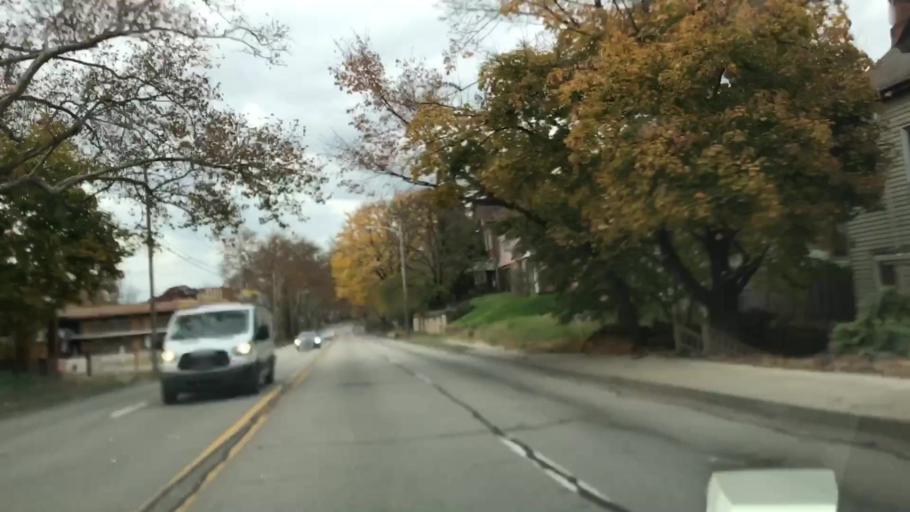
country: US
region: Pennsylvania
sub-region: Allegheny County
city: Avalon
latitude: 40.4992
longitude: -80.0715
